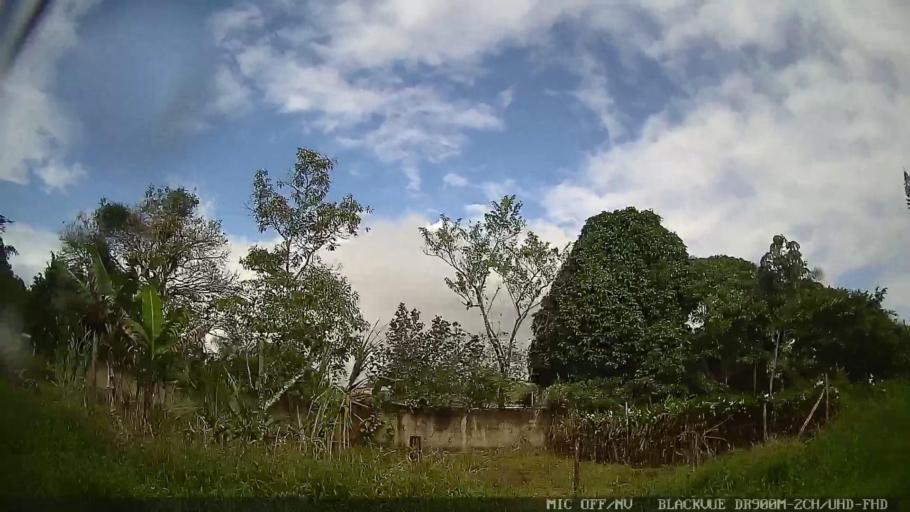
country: BR
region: Sao Paulo
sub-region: Itanhaem
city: Itanhaem
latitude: -24.2250
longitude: -46.9009
